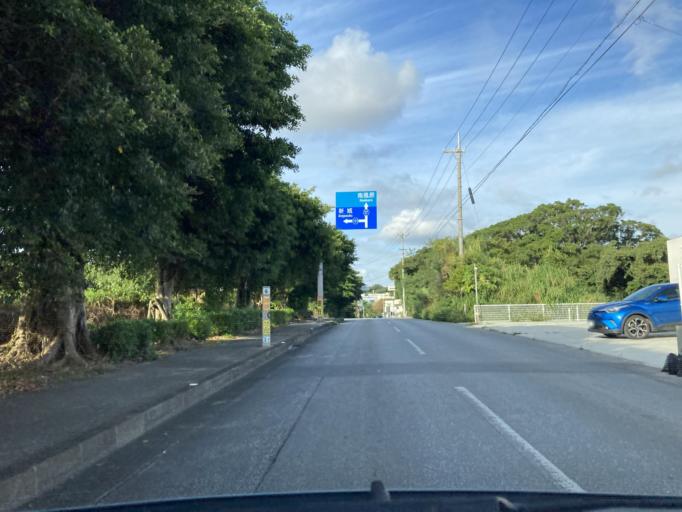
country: JP
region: Okinawa
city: Itoman
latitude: 26.1395
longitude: 127.7471
